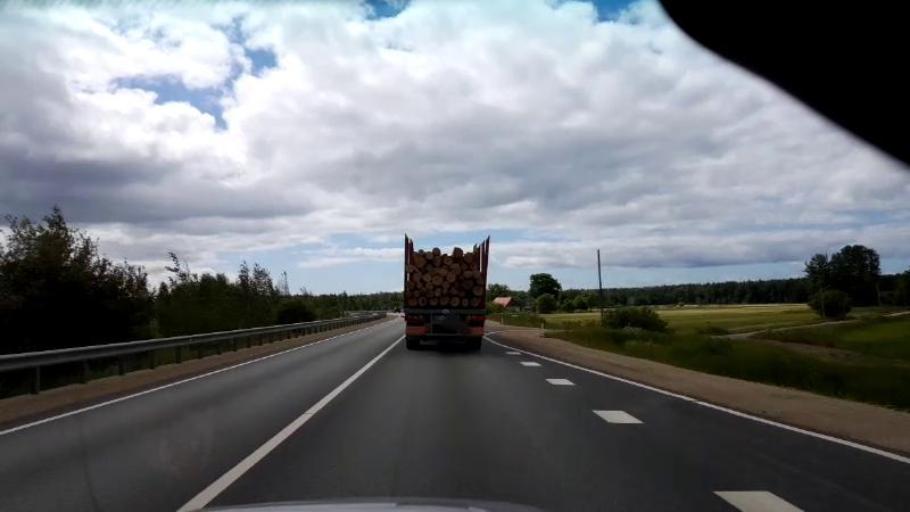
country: LV
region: Salacgrivas
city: Salacgriva
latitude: 57.7186
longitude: 24.3632
